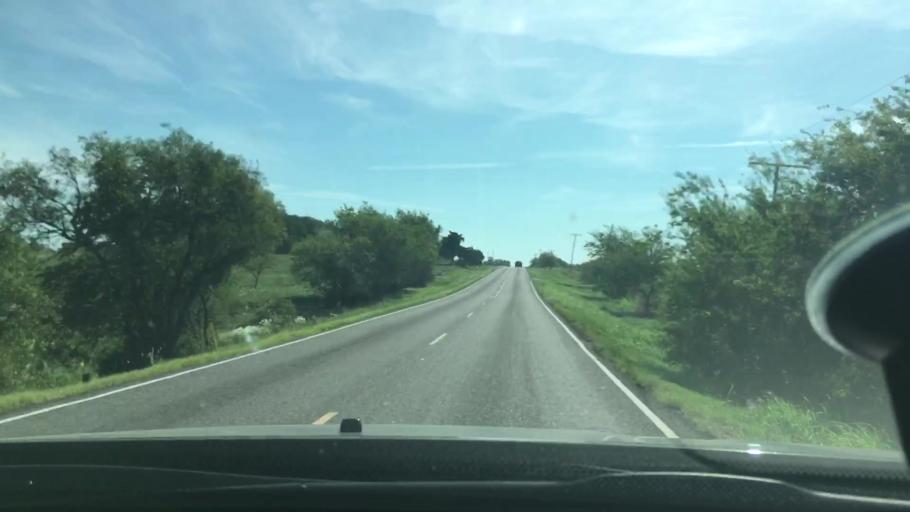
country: US
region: Oklahoma
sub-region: Carter County
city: Ardmore
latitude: 34.3327
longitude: -97.1969
